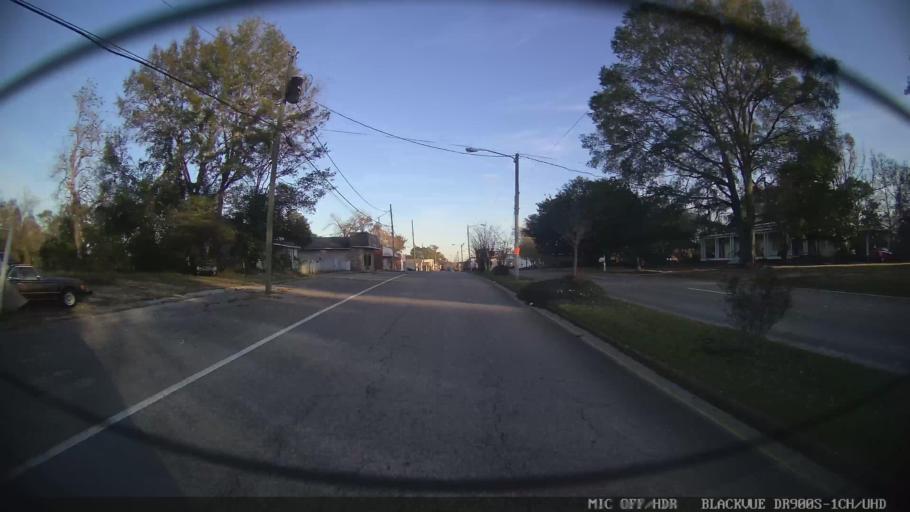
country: US
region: Mississippi
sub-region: Lamar County
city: Lumberton
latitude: 31.0024
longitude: -89.4547
